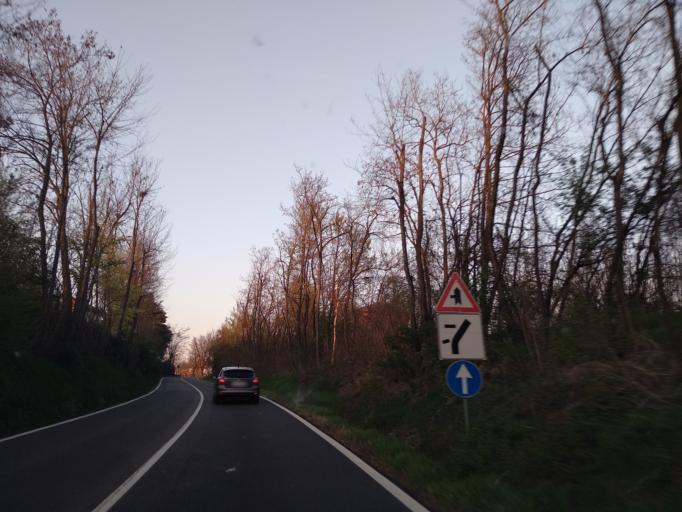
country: IT
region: Emilia-Romagna
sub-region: Provincia di Reggio Emilia
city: Puianello
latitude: 44.6291
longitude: 10.5695
